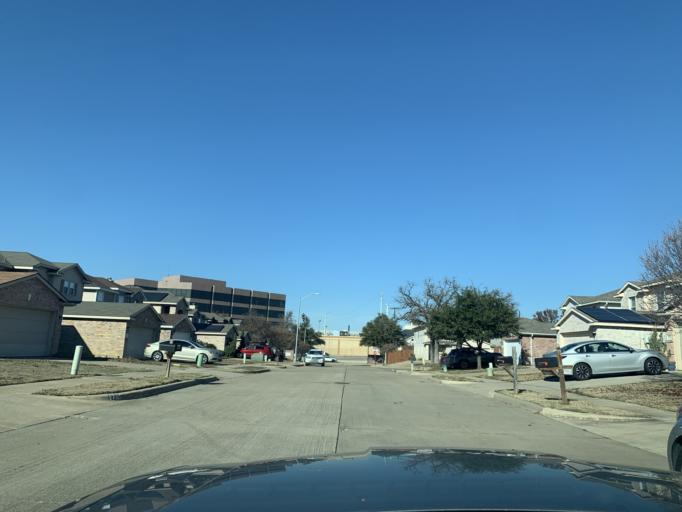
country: US
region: Texas
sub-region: Tarrant County
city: Bedford
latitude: 32.8344
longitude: -97.1408
